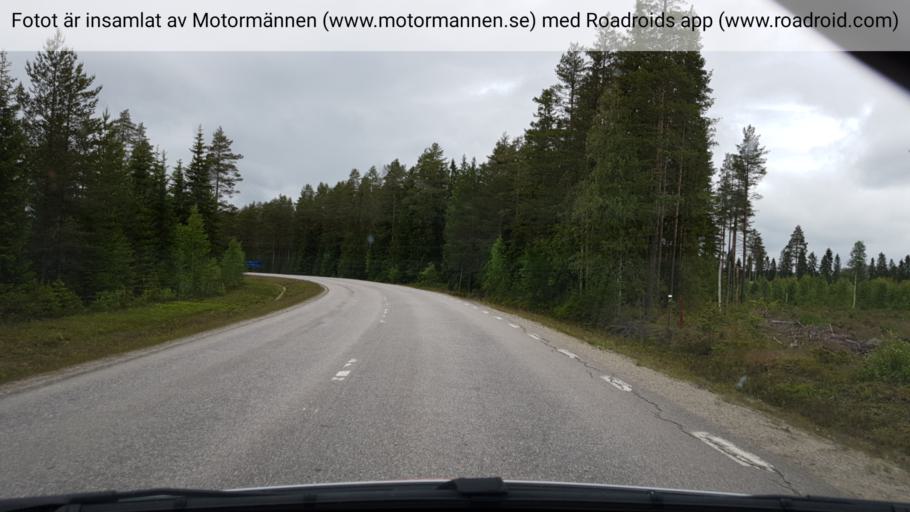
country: SE
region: Vaesterbotten
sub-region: Vindelns Kommun
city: Vindeln
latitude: 64.0803
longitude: 19.6332
